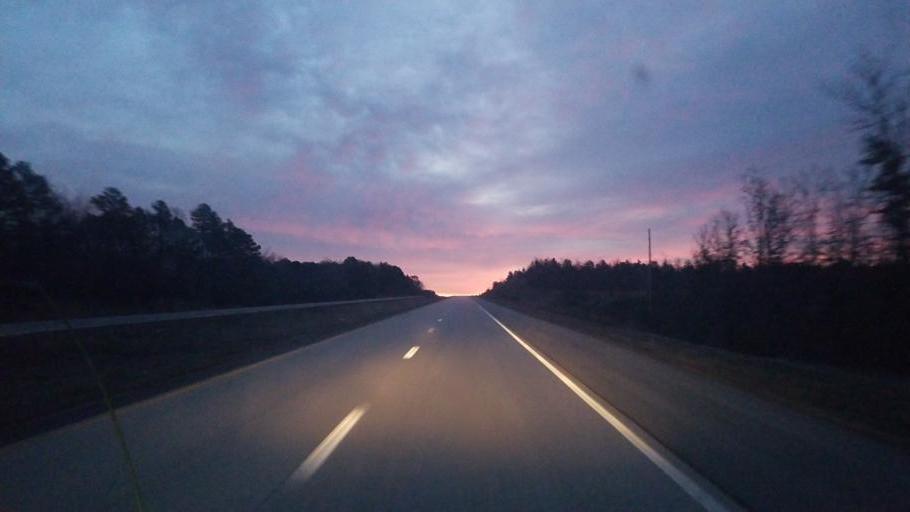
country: US
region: Missouri
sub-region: Shannon County
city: Winona
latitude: 36.9984
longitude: -91.4090
